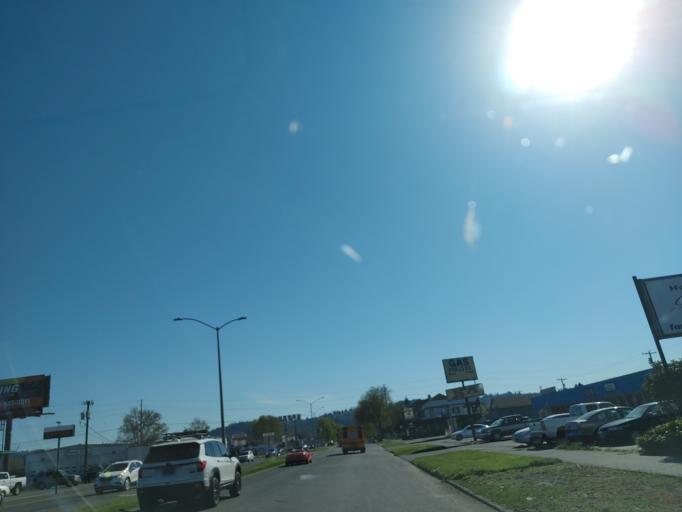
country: US
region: Washington
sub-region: Cowlitz County
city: Longview
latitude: 46.1228
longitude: -122.9450
